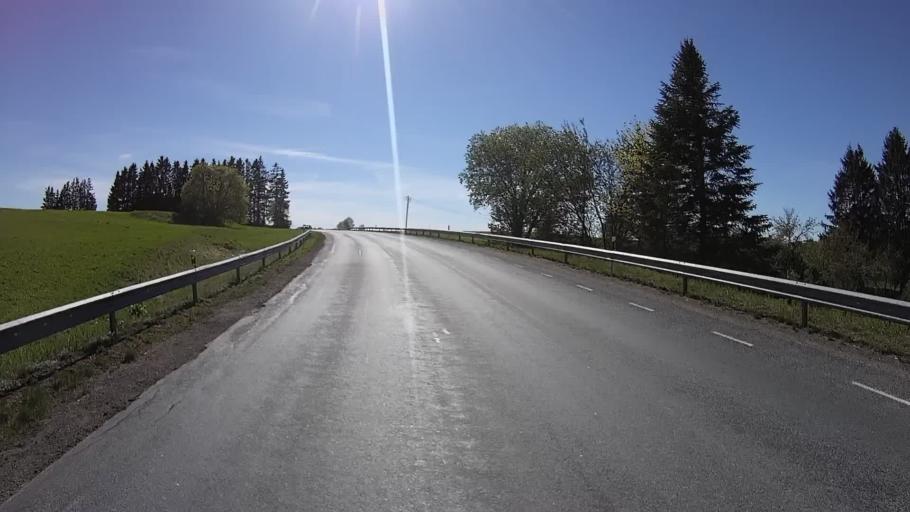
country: EE
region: Harju
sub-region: Loksa linn
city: Loksa
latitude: 59.5282
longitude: 25.7039
